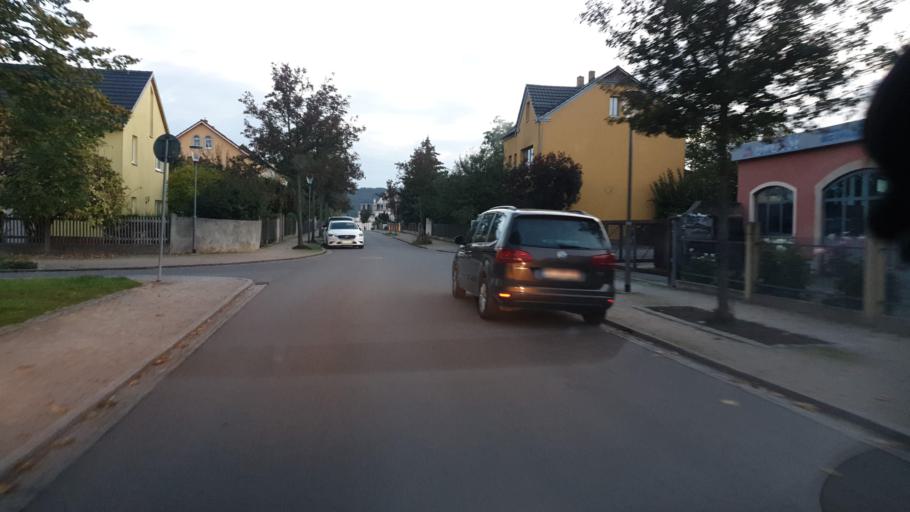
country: DE
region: Saxony
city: Radebeul
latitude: 51.1057
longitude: 13.6233
